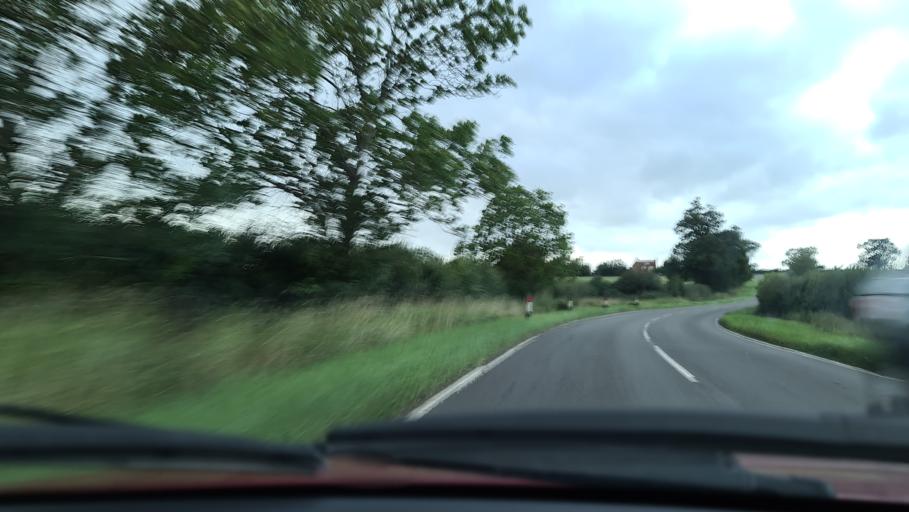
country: GB
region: England
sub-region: Buckinghamshire
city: Long Crendon
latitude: 51.7908
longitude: -1.0241
